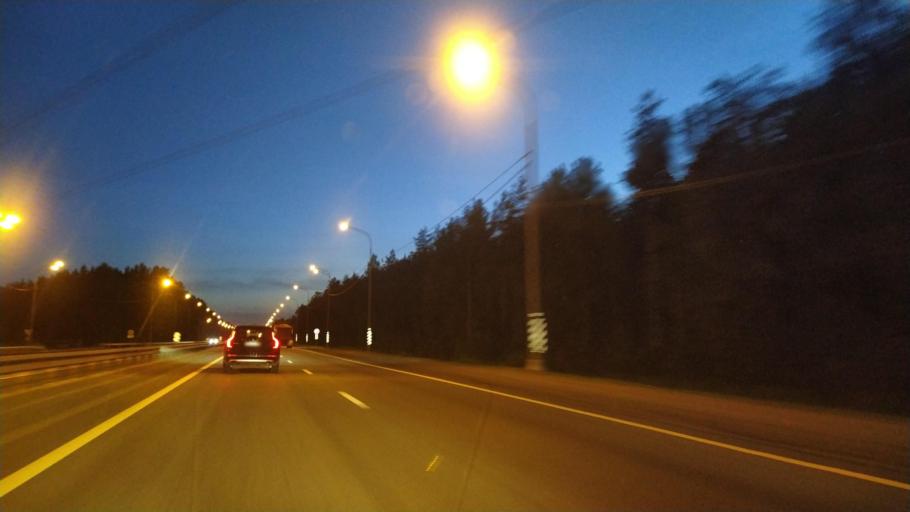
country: RU
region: Leningrad
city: Yanino Vtoroye
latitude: 59.8914
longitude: 30.5572
